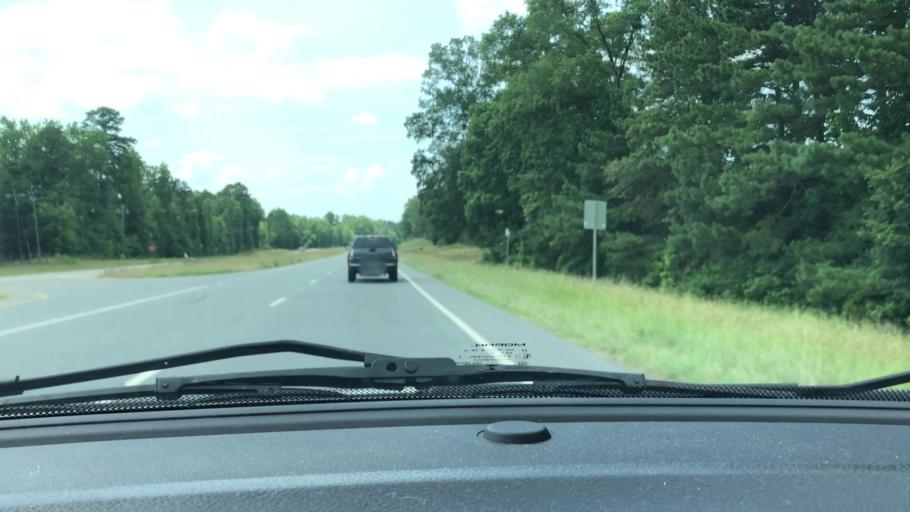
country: US
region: North Carolina
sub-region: Chatham County
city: Farmville
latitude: 35.5253
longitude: -79.2275
